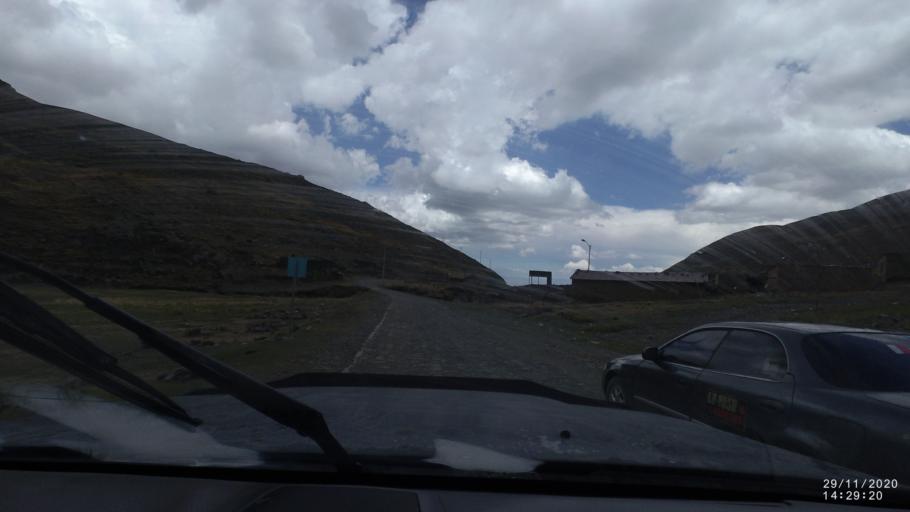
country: BO
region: Cochabamba
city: Sipe Sipe
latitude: -17.2612
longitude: -66.3557
